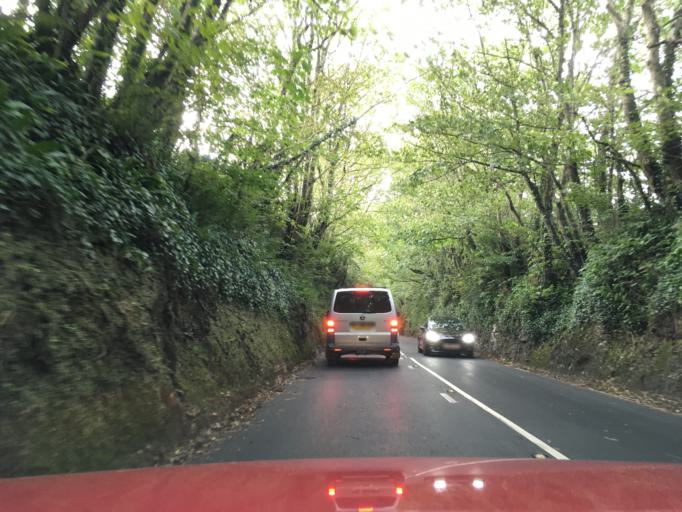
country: GB
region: England
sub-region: Devon
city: Modbury
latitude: 50.3502
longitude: -3.9056
